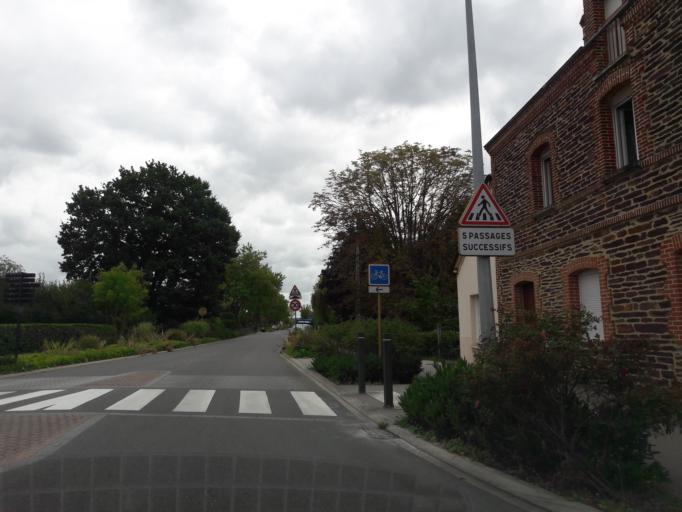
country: FR
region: Brittany
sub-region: Departement d'Ille-et-Vilaine
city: Chartres-de-Bretagne
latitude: 48.0131
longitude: -1.7025
